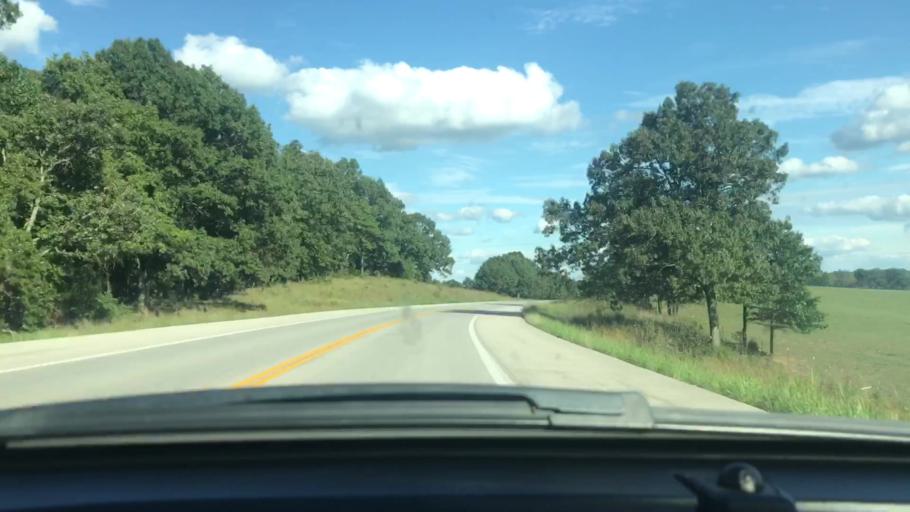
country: US
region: Missouri
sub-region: Howell County
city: West Plains
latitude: 36.6608
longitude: -91.7095
